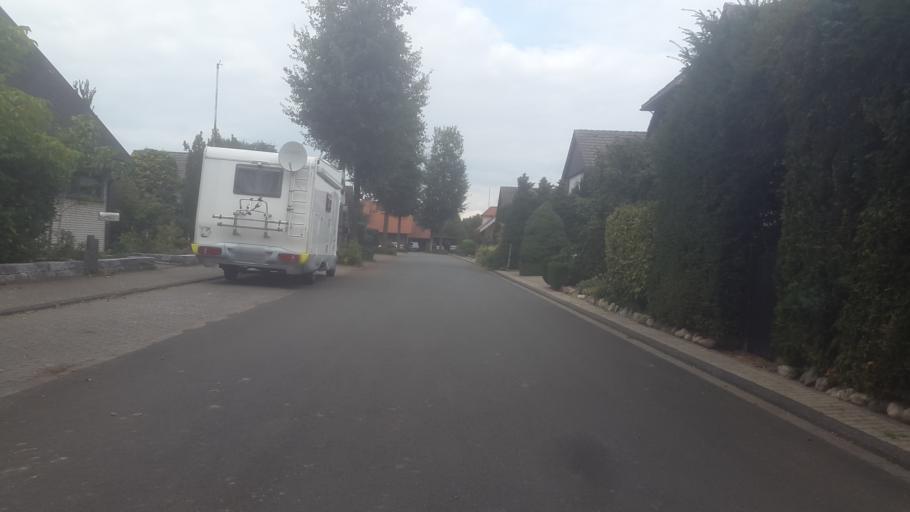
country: DE
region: North Rhine-Westphalia
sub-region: Regierungsbezirk Munster
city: Everswinkel
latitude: 51.9755
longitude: 7.9028
